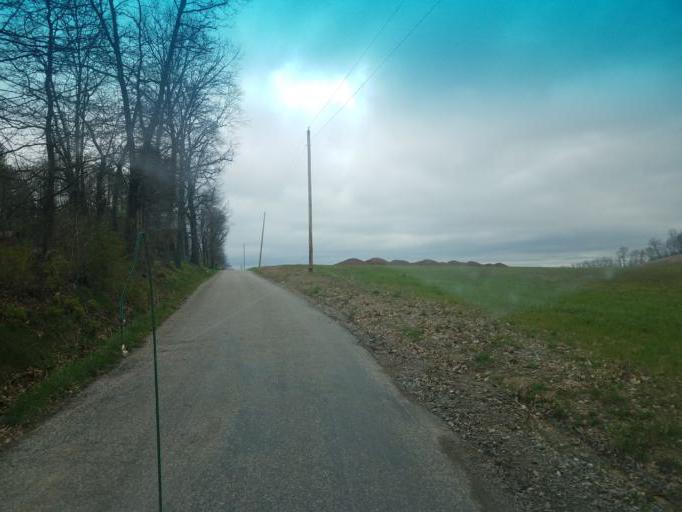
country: US
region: Ohio
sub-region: Stark County
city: Beach City
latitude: 40.6142
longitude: -81.6716
